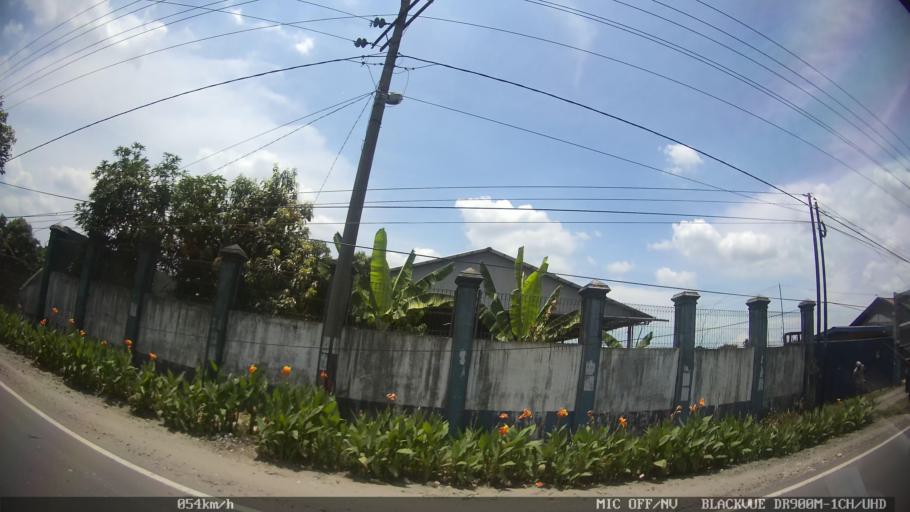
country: ID
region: North Sumatra
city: Binjai
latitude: 3.6024
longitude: 98.5389
